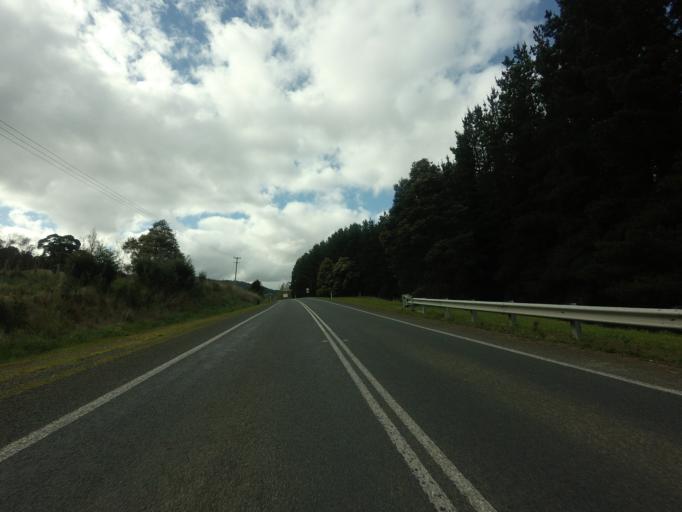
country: AU
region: Tasmania
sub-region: Huon Valley
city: Franklin
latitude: -43.1258
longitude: 146.9892
